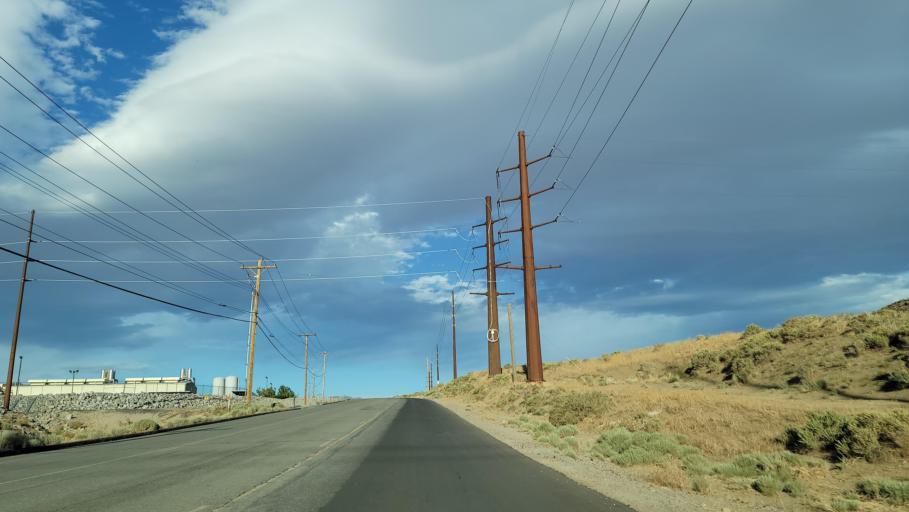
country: US
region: Nevada
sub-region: Washoe County
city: Spanish Springs
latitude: 39.5591
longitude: -119.5135
